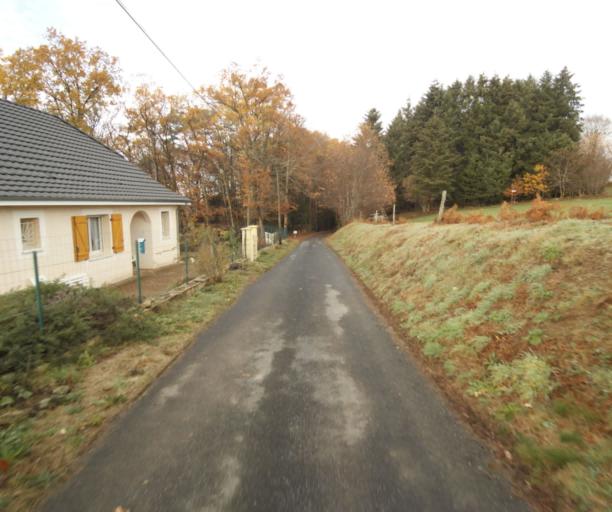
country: FR
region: Limousin
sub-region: Departement de la Correze
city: Cornil
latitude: 45.1998
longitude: 1.7122
